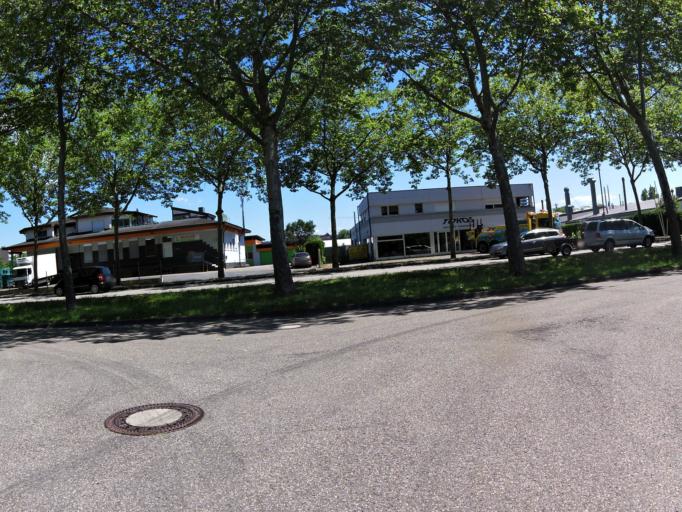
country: DE
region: Baden-Wuerttemberg
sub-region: Freiburg Region
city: Lahr
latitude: 48.3386
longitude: 7.8309
